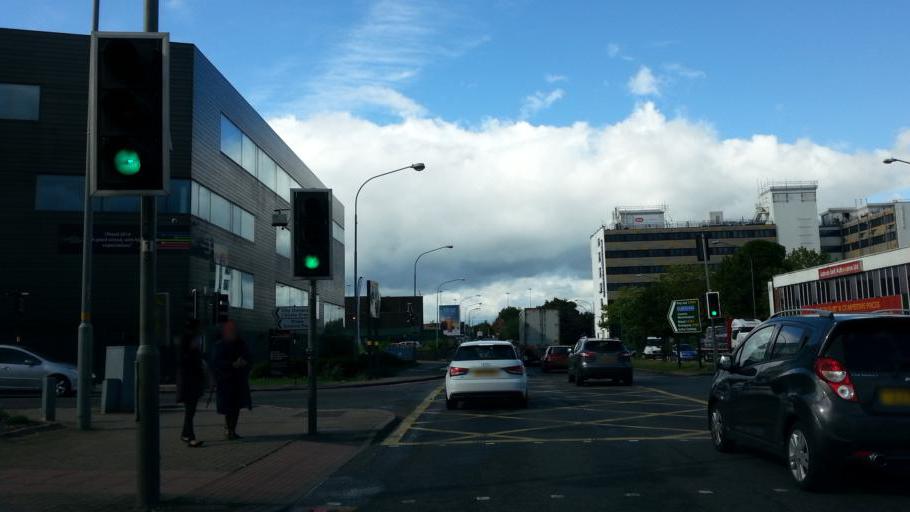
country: GB
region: England
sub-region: City and Borough of Birmingham
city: Birmingham
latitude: 52.4889
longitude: -1.8852
